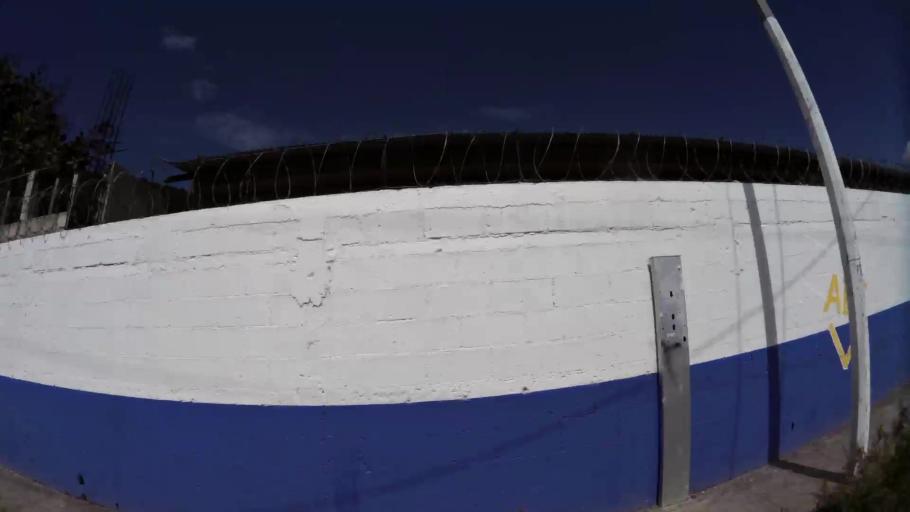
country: GT
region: Solola
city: Panajachel
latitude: 14.7418
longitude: -91.1591
